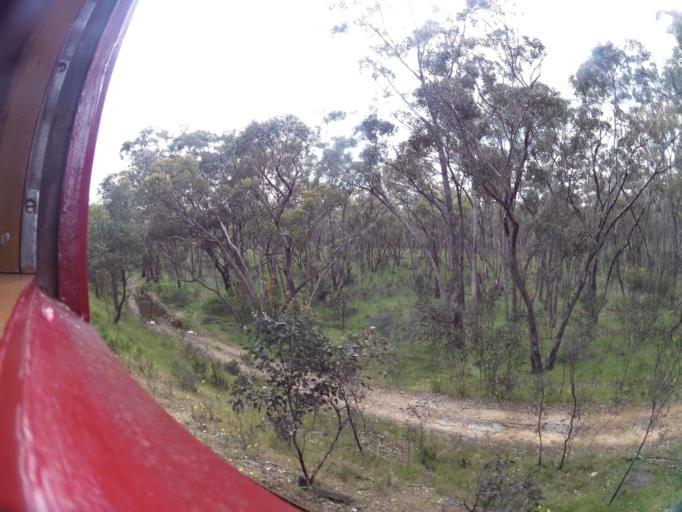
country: AU
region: Victoria
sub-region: Mount Alexander
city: Castlemaine
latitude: -37.0046
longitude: 144.1131
